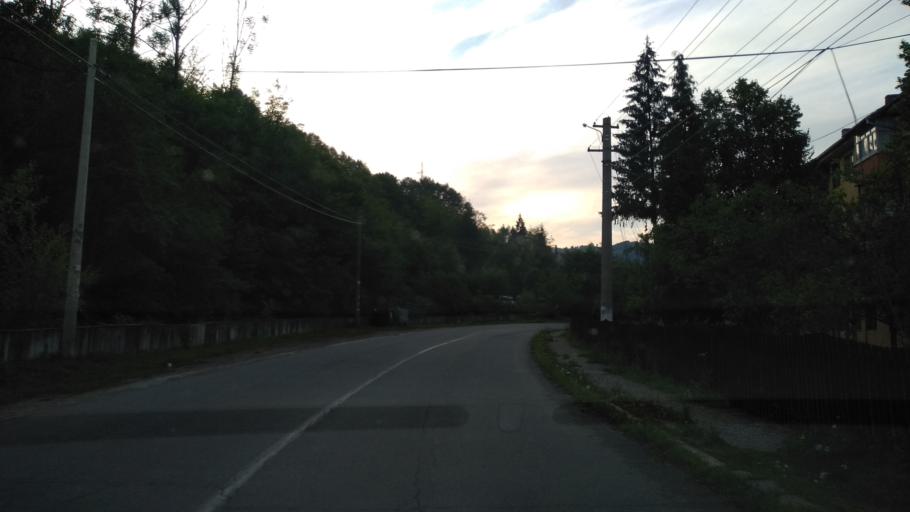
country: RO
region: Hunedoara
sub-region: Comuna Aninoasa
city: Aninoasa
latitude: 45.3910
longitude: 23.3191
